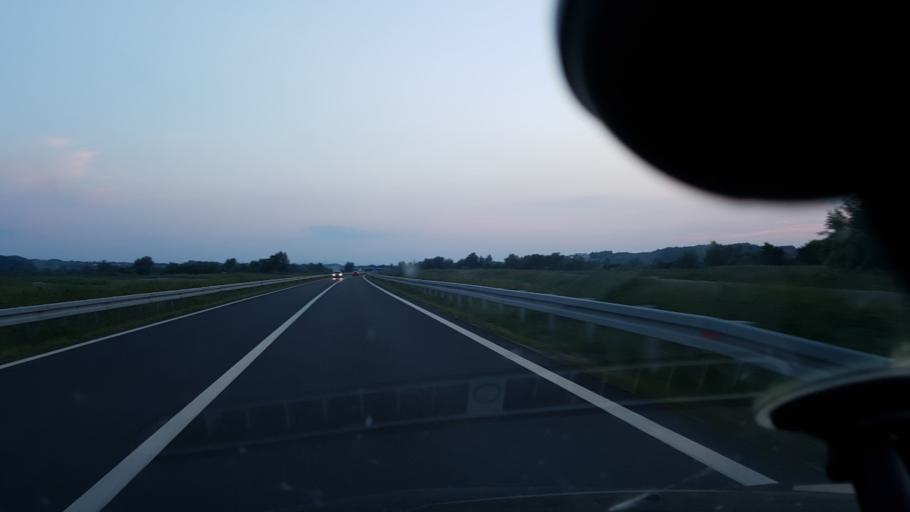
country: HR
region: Krapinsko-Zagorska
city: Bedekovcina
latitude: 46.0223
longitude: 15.9687
